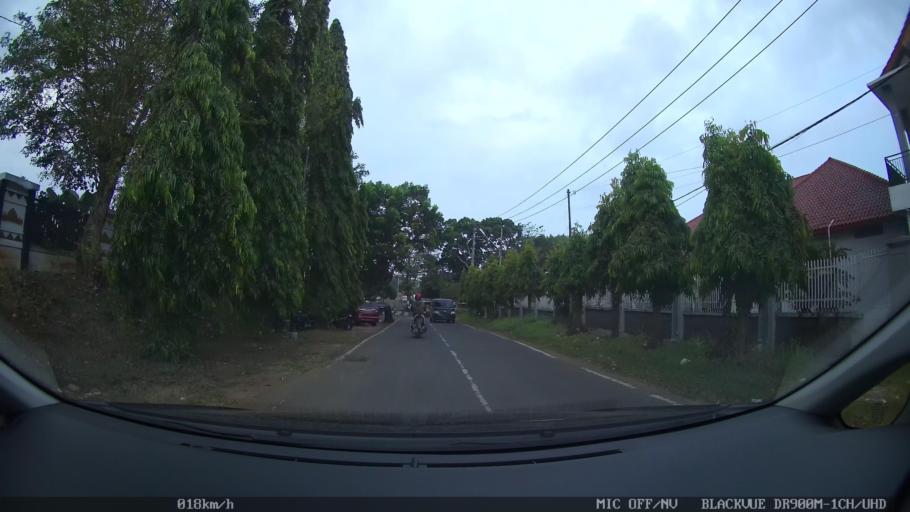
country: ID
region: Lampung
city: Bandarlampung
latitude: -5.4325
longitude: 105.2477
